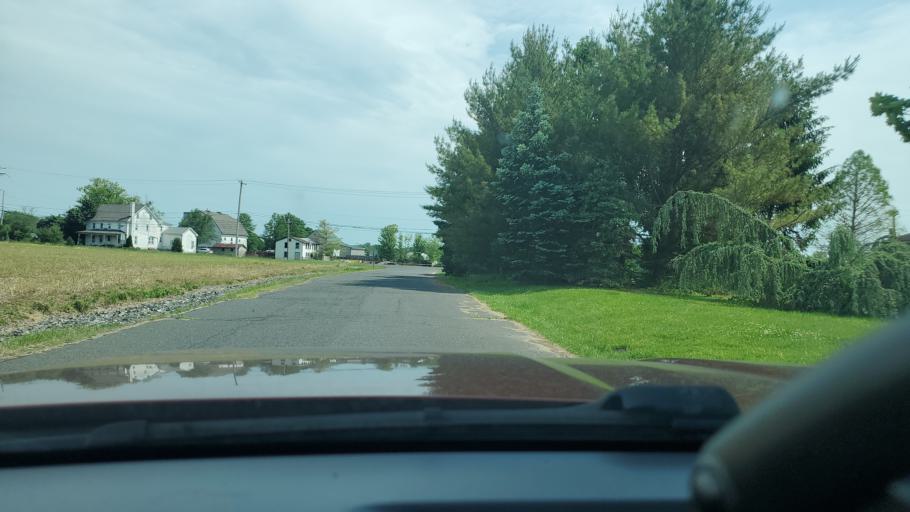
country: US
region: Pennsylvania
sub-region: Montgomery County
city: Spring Mount
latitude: 40.2865
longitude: -75.5119
